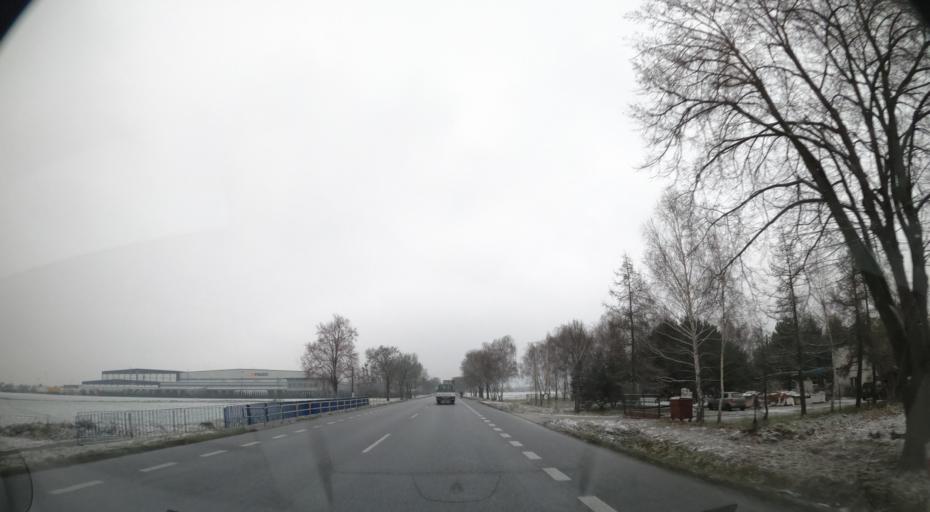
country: PL
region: Masovian Voivodeship
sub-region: Powiat warszawski zachodni
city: Bieniewice
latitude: 52.2050
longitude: 20.5056
